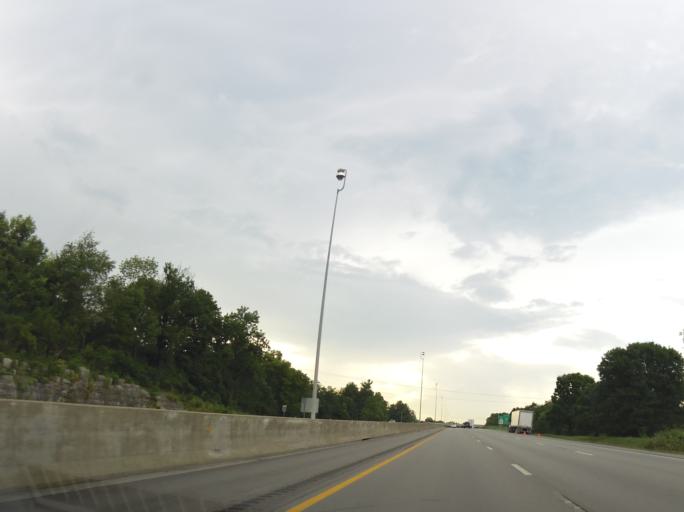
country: US
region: Kentucky
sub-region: Madison County
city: Richmond
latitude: 37.8881
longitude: -84.3453
